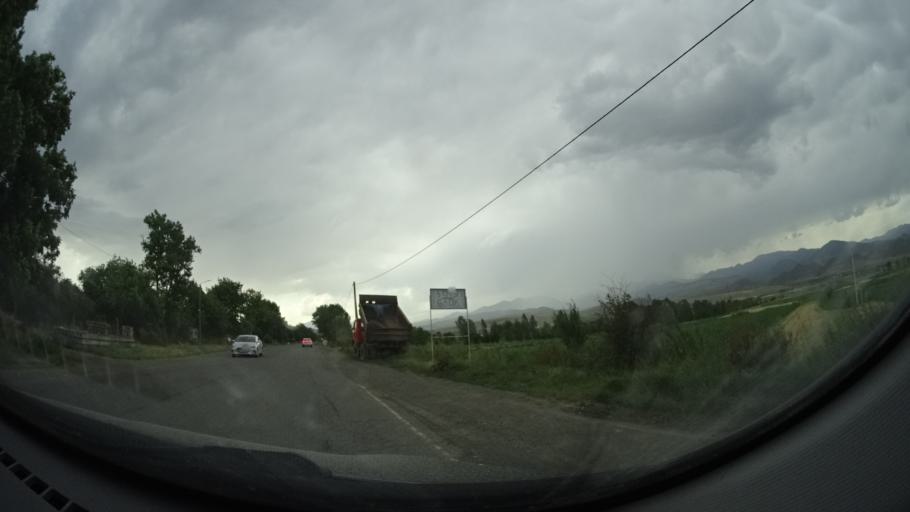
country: GE
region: Samtskhe-Javakheti
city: Akhaltsikhe
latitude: 41.6373
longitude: 43.0373
